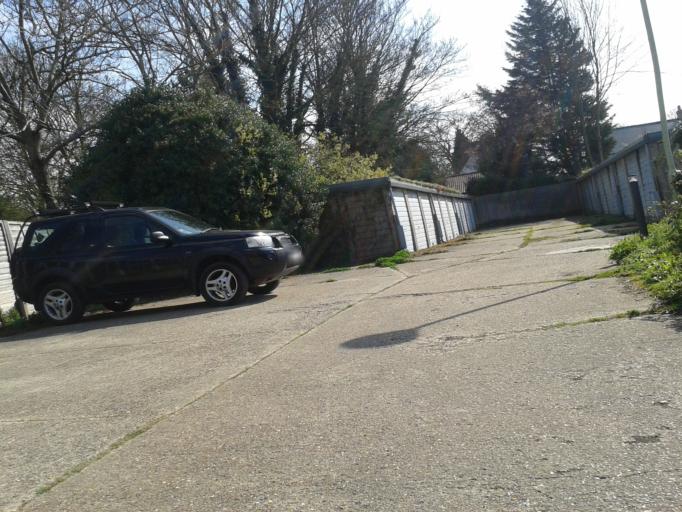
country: GB
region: England
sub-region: Cambridgeshire
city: Sawston
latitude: 52.1533
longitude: 0.1442
